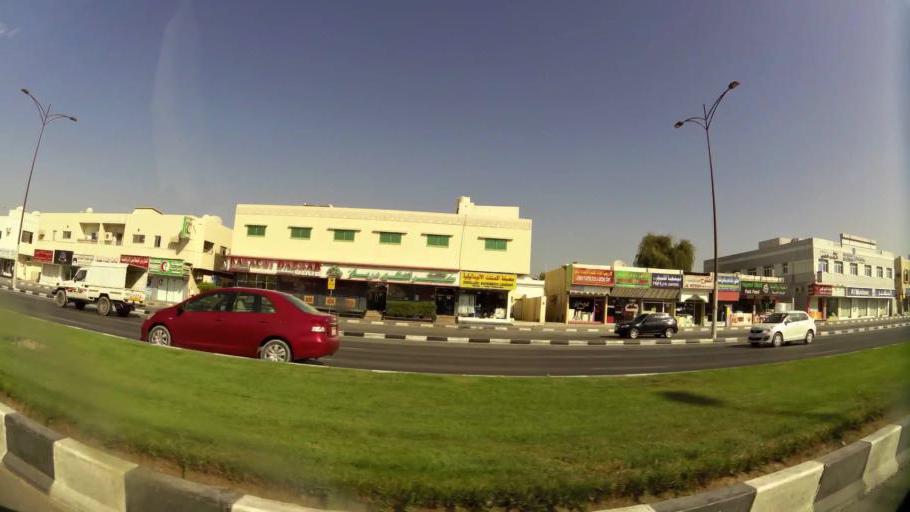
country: AE
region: Ash Shariqah
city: Sharjah
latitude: 25.3355
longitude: 55.4254
